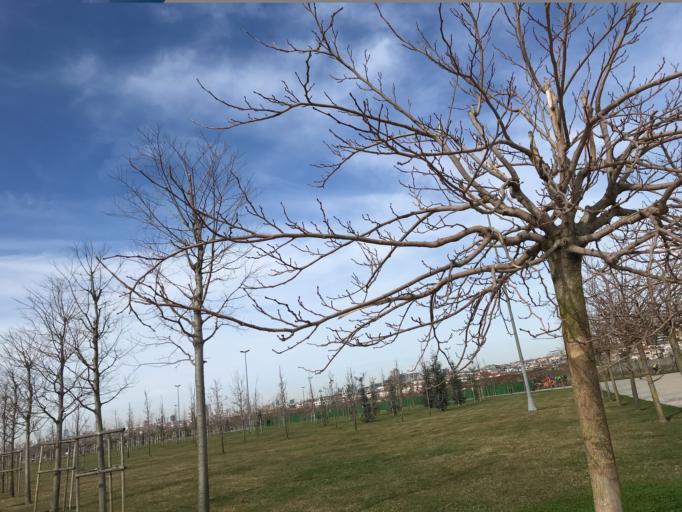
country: TR
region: Istanbul
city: Maltepe
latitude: 40.9294
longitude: 29.1151
